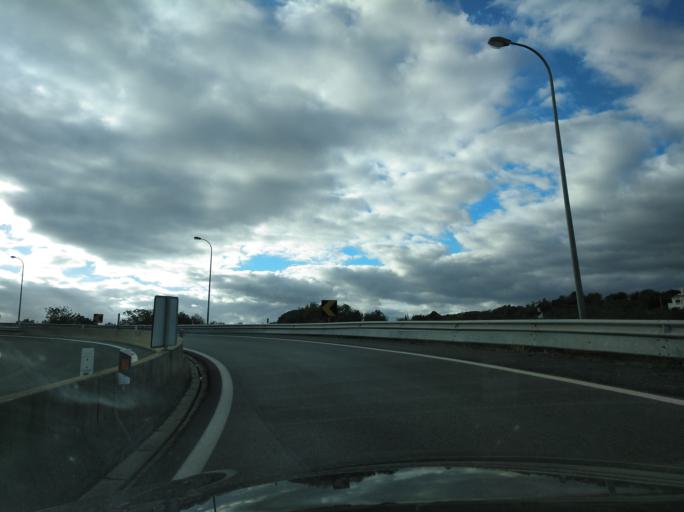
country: PT
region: Faro
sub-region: Tavira
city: Luz
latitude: 37.1383
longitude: -7.6955
